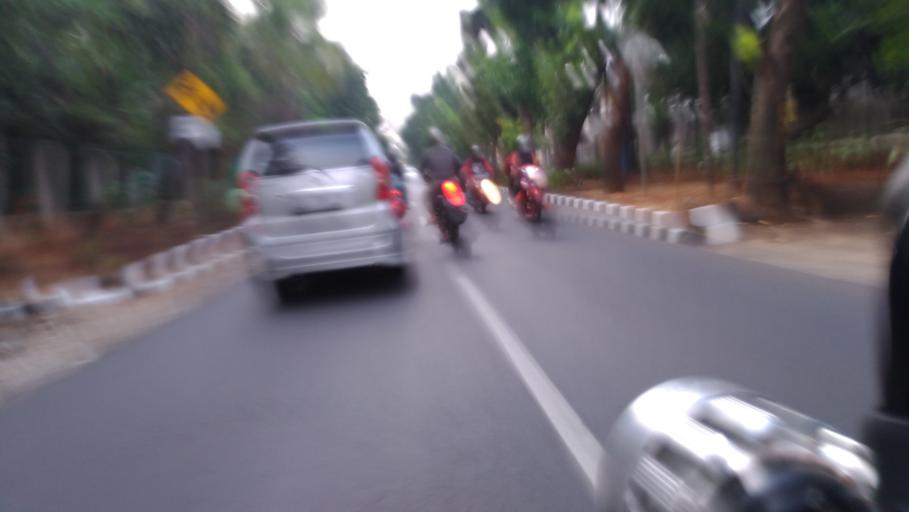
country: ID
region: West Java
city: Cileungsir
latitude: -6.3559
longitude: 106.8894
